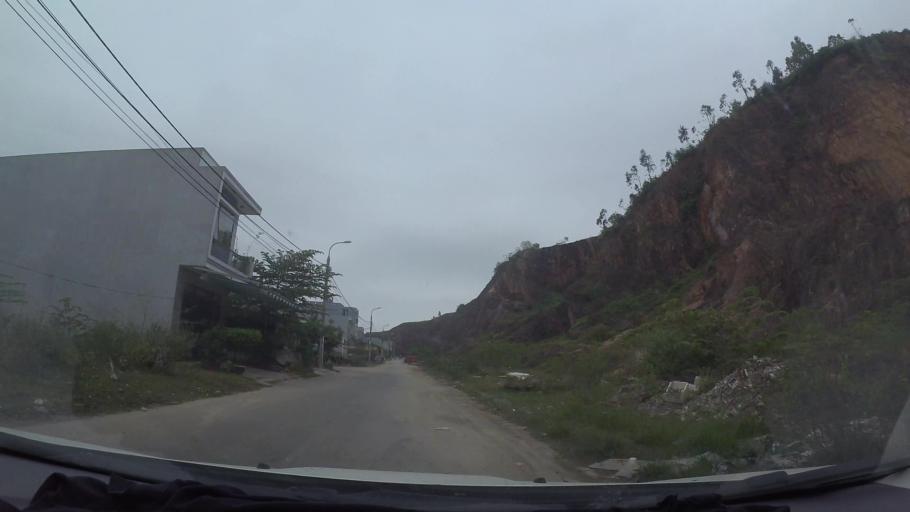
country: VN
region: Da Nang
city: Lien Chieu
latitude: 16.0653
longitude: 108.1450
